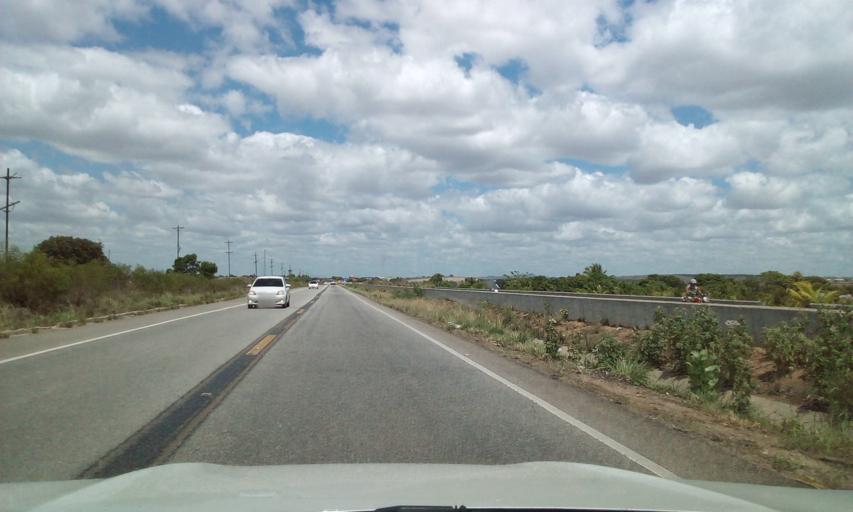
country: BR
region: Alagoas
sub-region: Porto Real Do Colegio
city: Porto Real do Colegio
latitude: -10.1946
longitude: -36.8236
